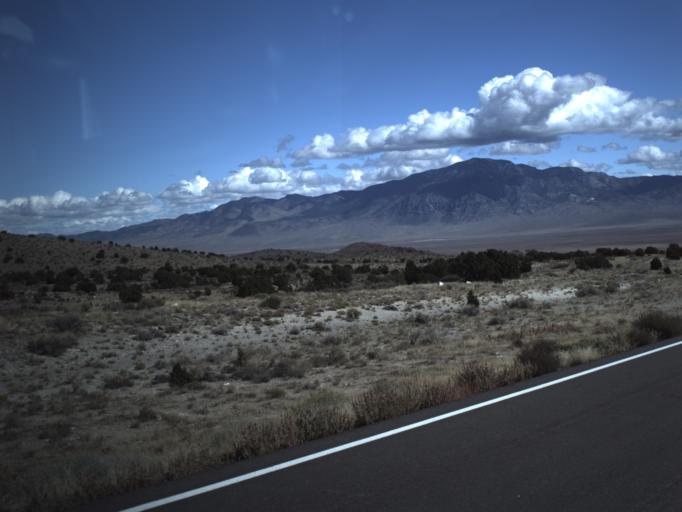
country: US
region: Utah
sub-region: Beaver County
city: Milford
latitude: 38.5019
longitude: -113.5038
